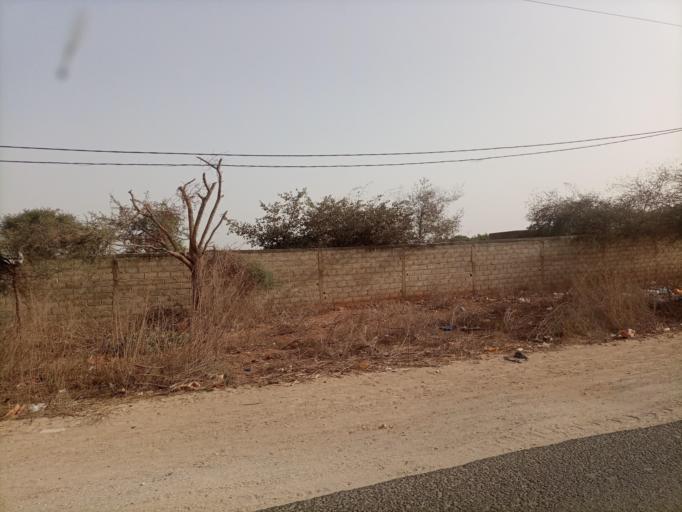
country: SN
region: Thies
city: Nguekhokh
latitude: 14.5866
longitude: -17.0255
